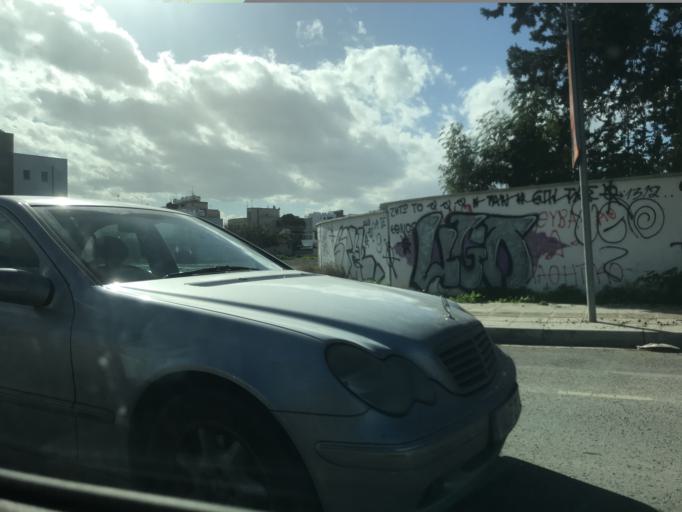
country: CY
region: Lefkosia
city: Nicosia
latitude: 35.1659
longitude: 33.3818
